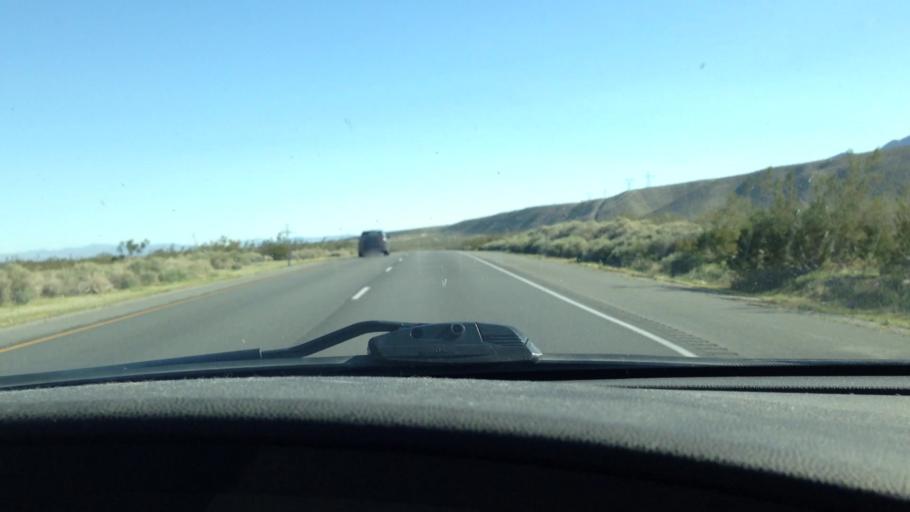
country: US
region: California
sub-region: Kern County
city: Inyokern
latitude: 35.8973
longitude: -117.8990
